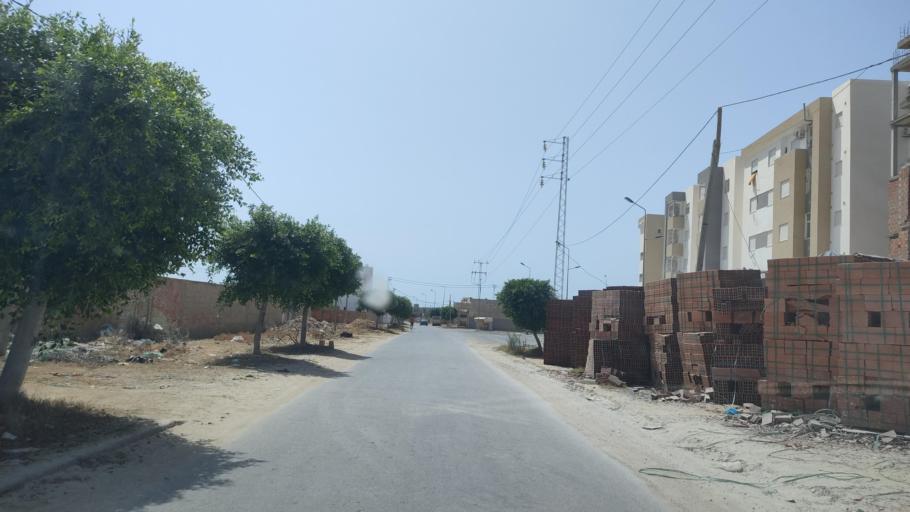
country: TN
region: Safaqis
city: Sfax
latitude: 34.6693
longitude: 10.7065
